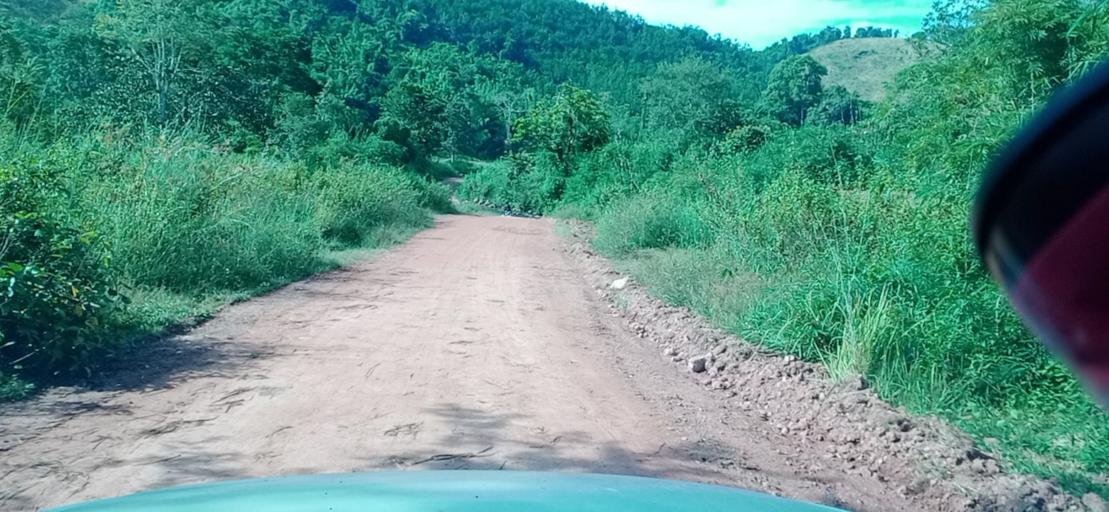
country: TH
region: Changwat Bueng Kan
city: Pak Khat
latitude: 18.6681
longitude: 103.2015
